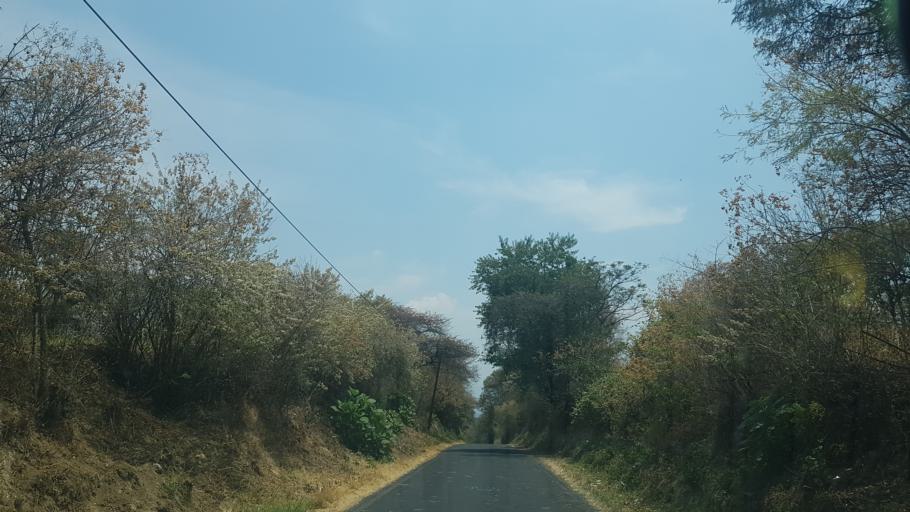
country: MX
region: Puebla
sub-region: Tochimilco
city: La Magdalena Yancuitlalpan
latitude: 18.8868
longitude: -98.5985
